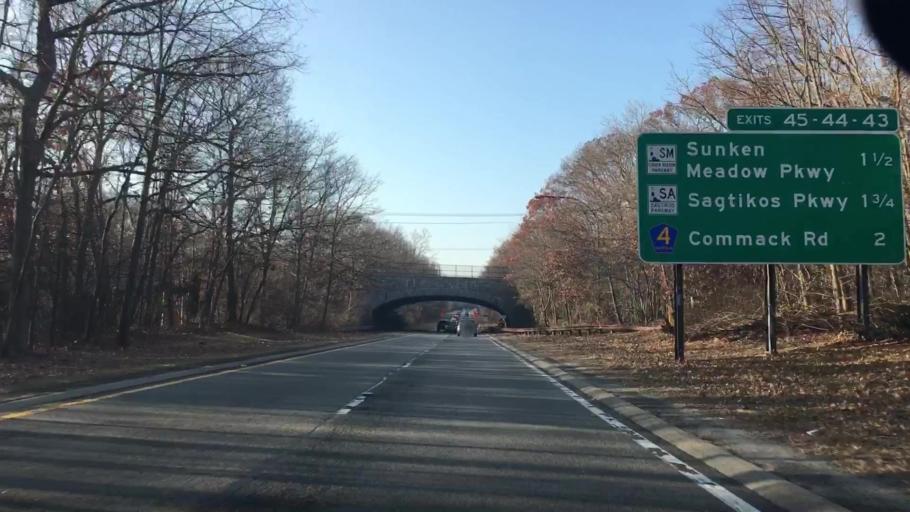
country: US
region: New York
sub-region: Suffolk County
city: Commack
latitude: 40.8252
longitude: -73.2619
